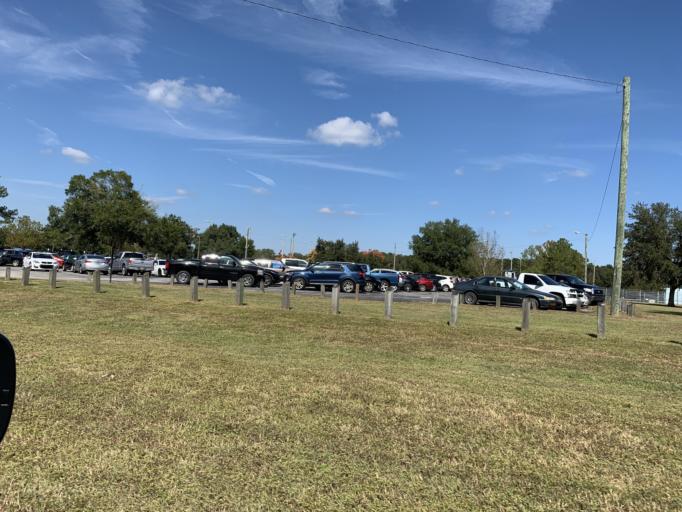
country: US
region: Florida
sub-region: Marion County
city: Ocala
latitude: 29.1643
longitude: -82.0884
